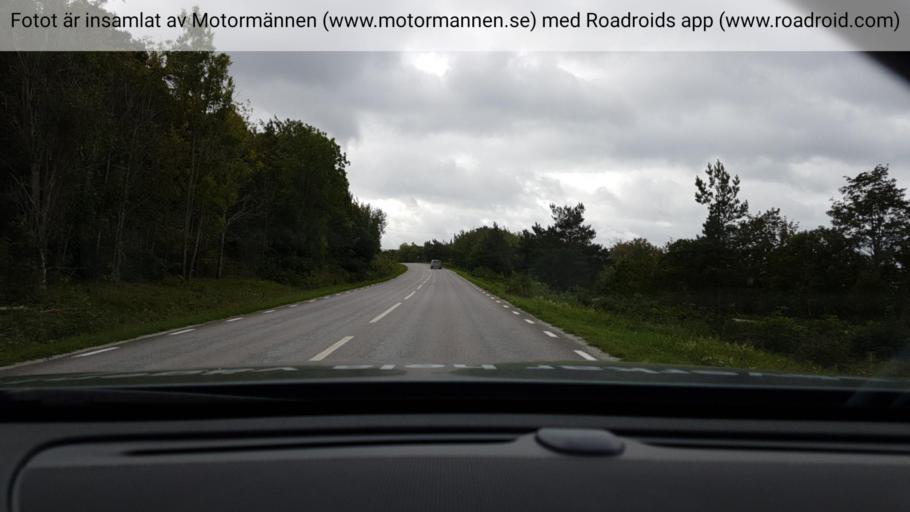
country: SE
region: Gotland
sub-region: Gotland
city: Klintehamn
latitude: 57.3407
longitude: 18.1910
